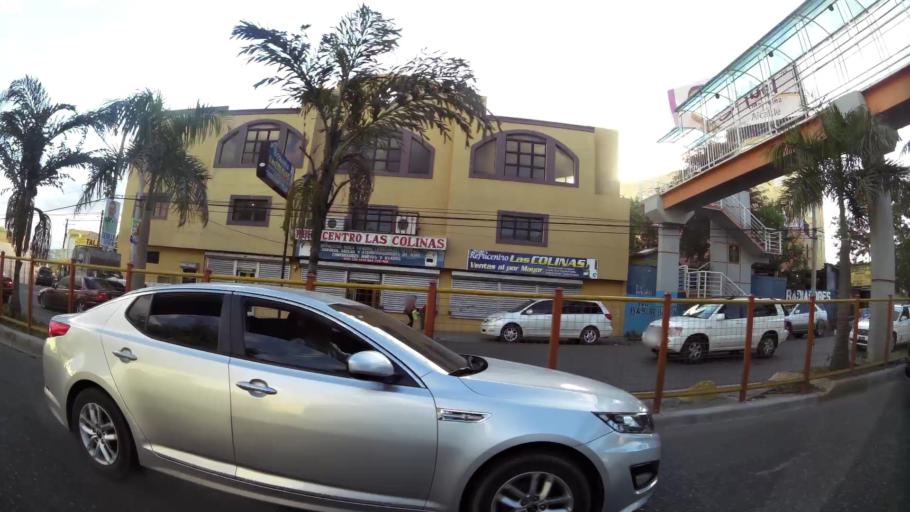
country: DO
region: Santiago
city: Santiago de los Caballeros
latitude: 19.4740
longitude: -70.7149
